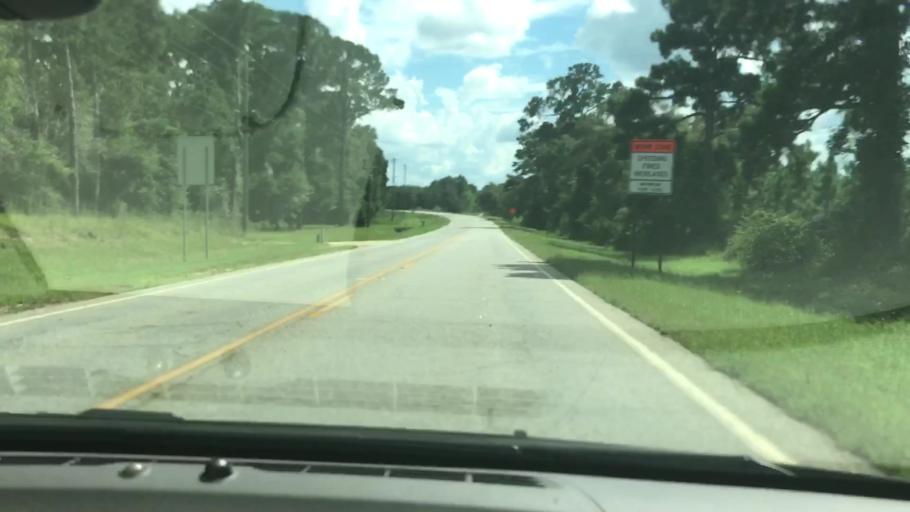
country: US
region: Georgia
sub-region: Clay County
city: Fort Gaines
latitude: 31.6557
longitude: -85.0474
